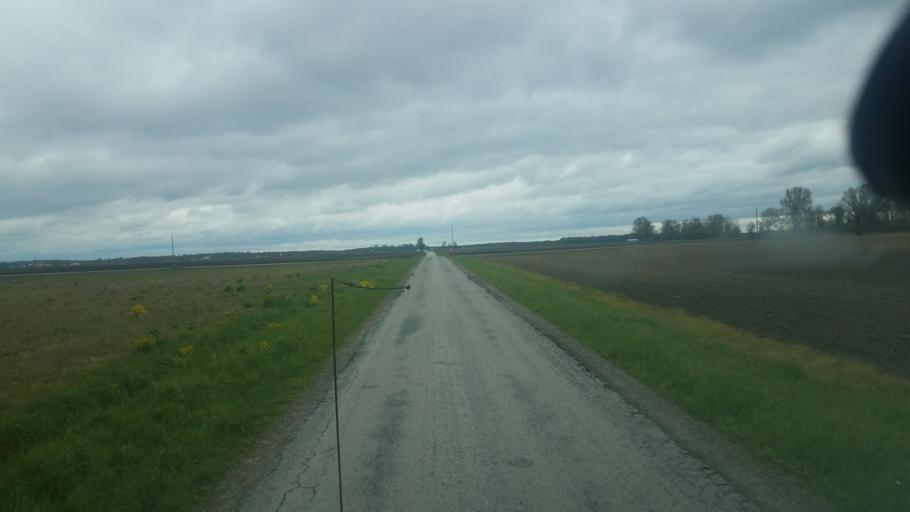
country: US
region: Ohio
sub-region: Crawford County
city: Bucyrus
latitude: 40.7154
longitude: -83.0733
